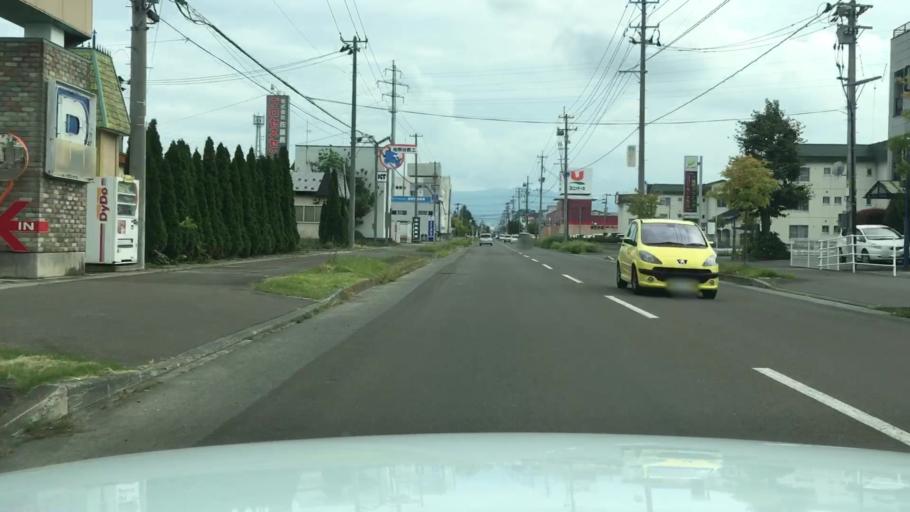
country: JP
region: Aomori
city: Hirosaki
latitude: 40.6244
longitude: 140.4852
